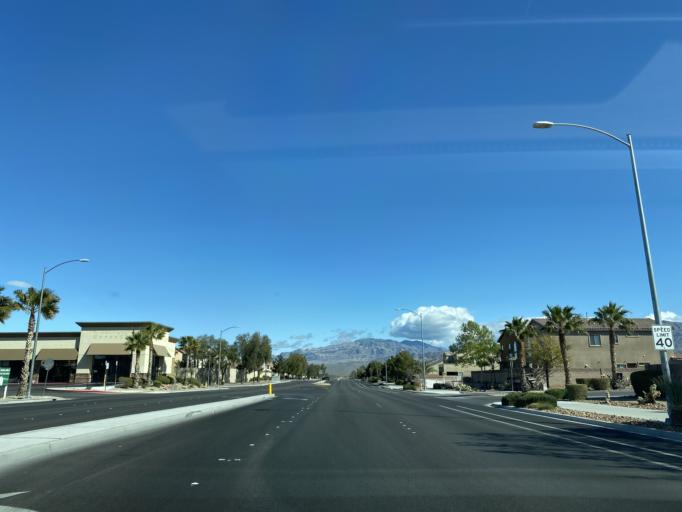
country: US
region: Nevada
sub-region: Clark County
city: Las Vegas
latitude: 36.3074
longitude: -115.2786
